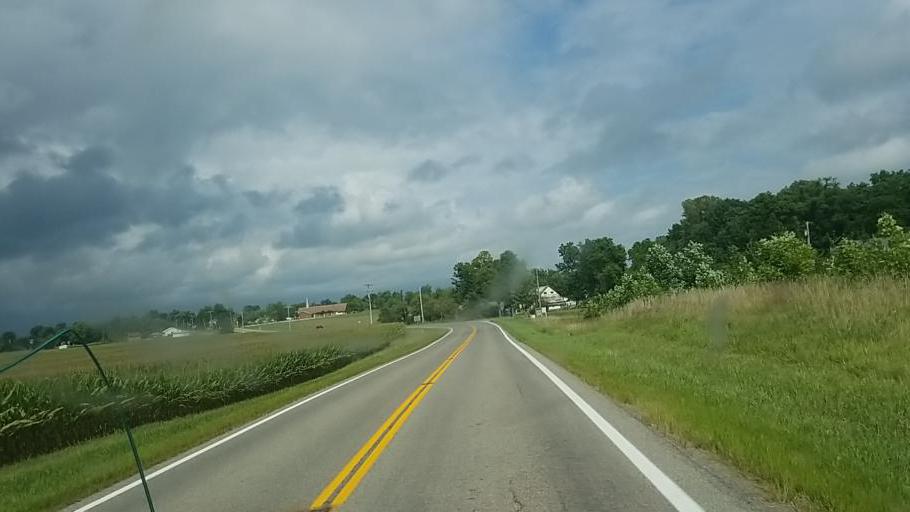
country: US
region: Ohio
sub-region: Champaign County
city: North Lewisburg
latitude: 40.2870
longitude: -83.5870
